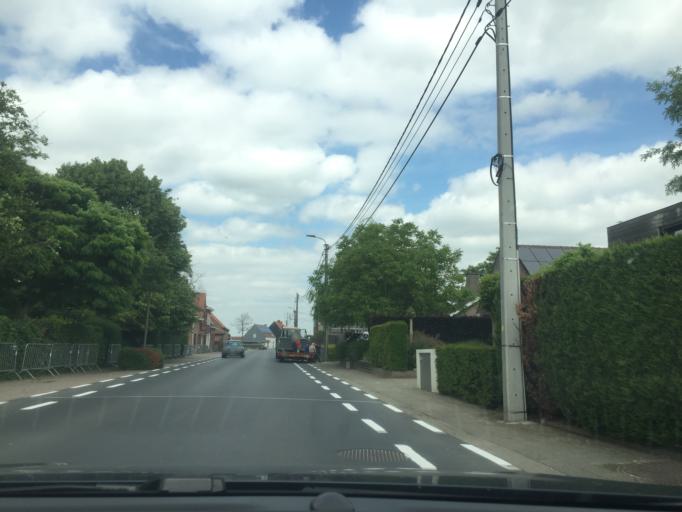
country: BE
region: Flanders
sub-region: Provincie West-Vlaanderen
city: Zwevegem
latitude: 50.7931
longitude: 3.3210
